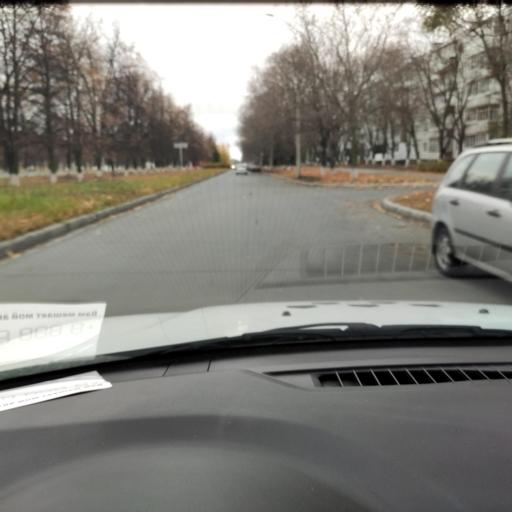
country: RU
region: Samara
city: Tol'yatti
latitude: 53.5196
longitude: 49.2878
